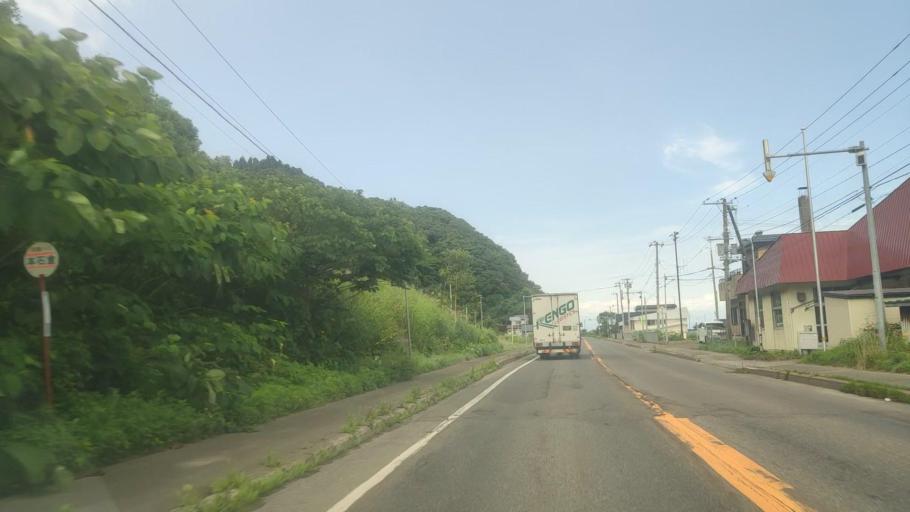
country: JP
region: Hokkaido
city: Nanae
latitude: 42.1603
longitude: 140.4716
